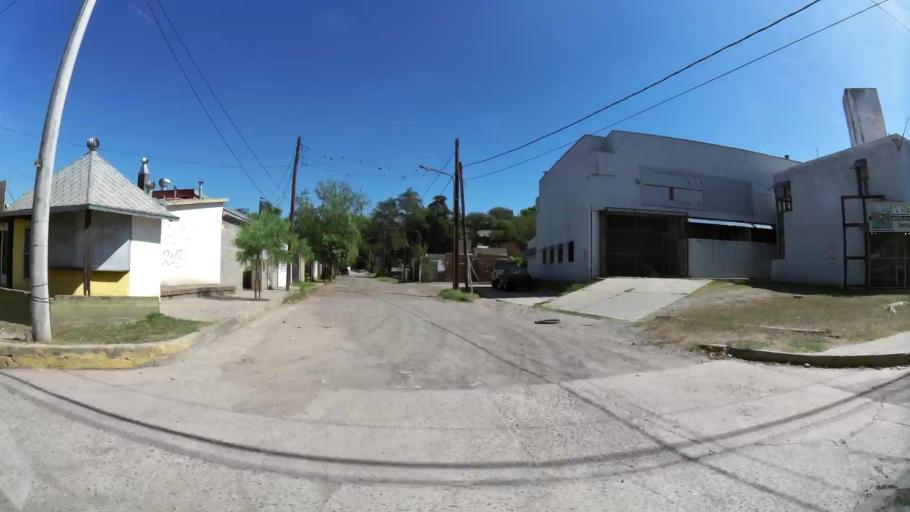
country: AR
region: Cordoba
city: Villa Allende
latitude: -31.2925
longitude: -64.3027
